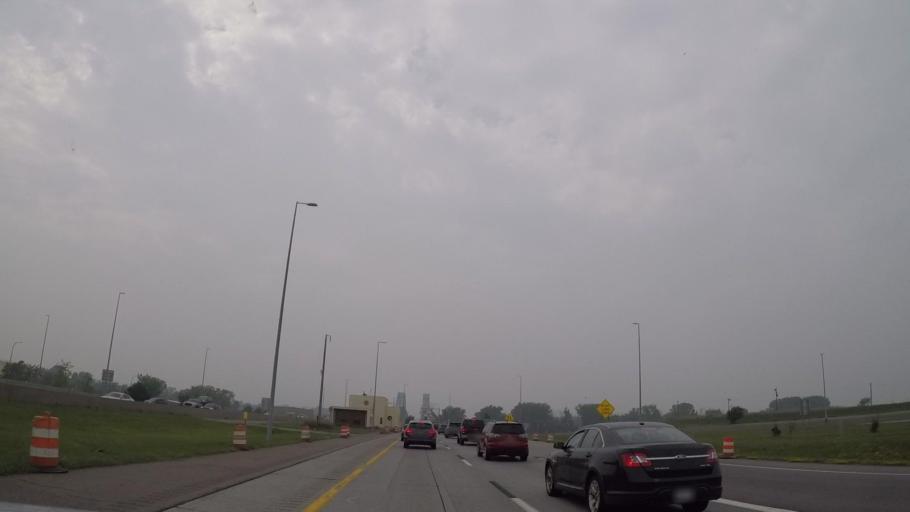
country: US
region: New York
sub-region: Erie County
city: Grandyle Village
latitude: 42.9937
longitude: -78.9280
